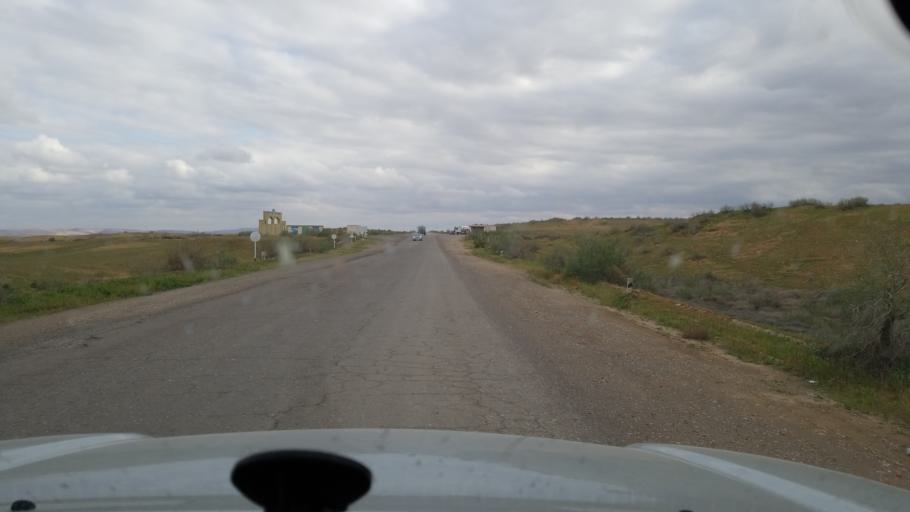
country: TM
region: Mary
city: Serhetabat
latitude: 35.9878
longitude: 62.6269
